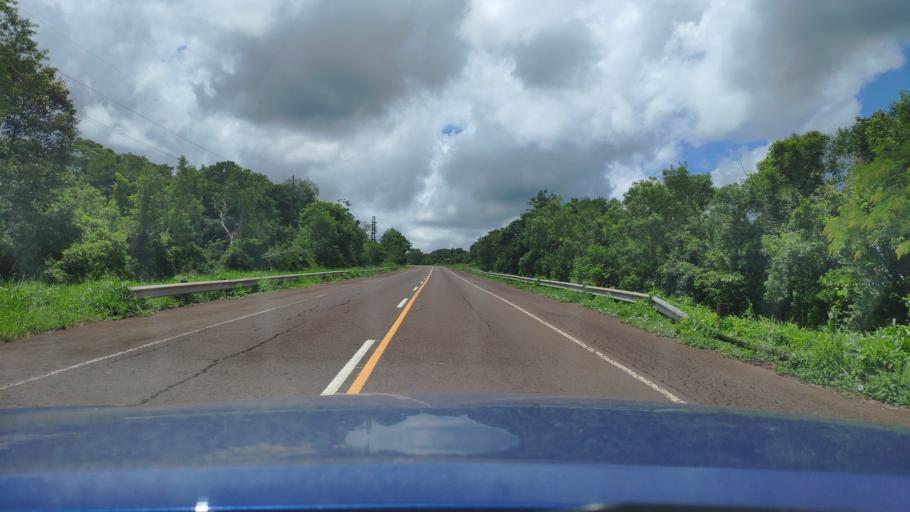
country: AR
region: Misiones
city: Dos Arroyos
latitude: -27.7570
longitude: -55.2470
